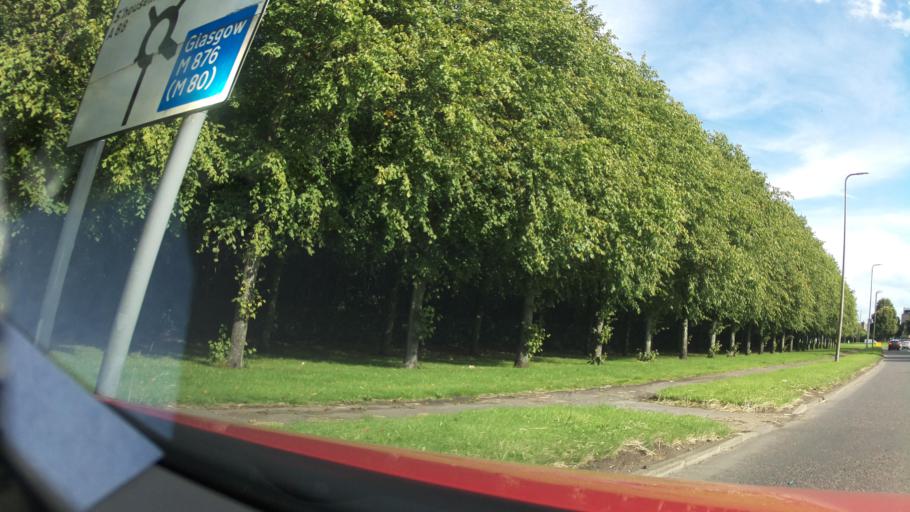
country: GB
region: Scotland
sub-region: Falkirk
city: Larbert
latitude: 56.0312
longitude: -3.8474
